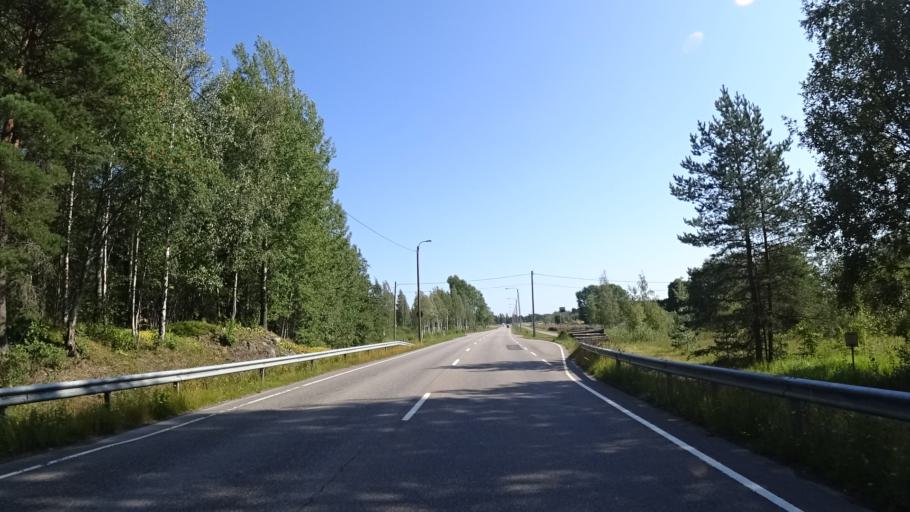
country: FI
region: Kymenlaakso
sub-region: Kotka-Hamina
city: Karhula
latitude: 60.5426
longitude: 26.9253
